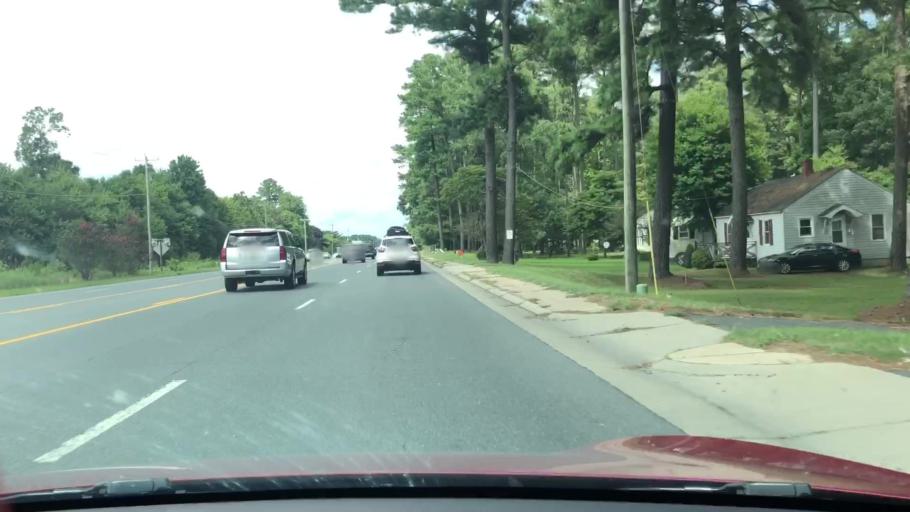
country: US
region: Virginia
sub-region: Accomack County
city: Wattsville
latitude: 37.8965
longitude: -75.5487
